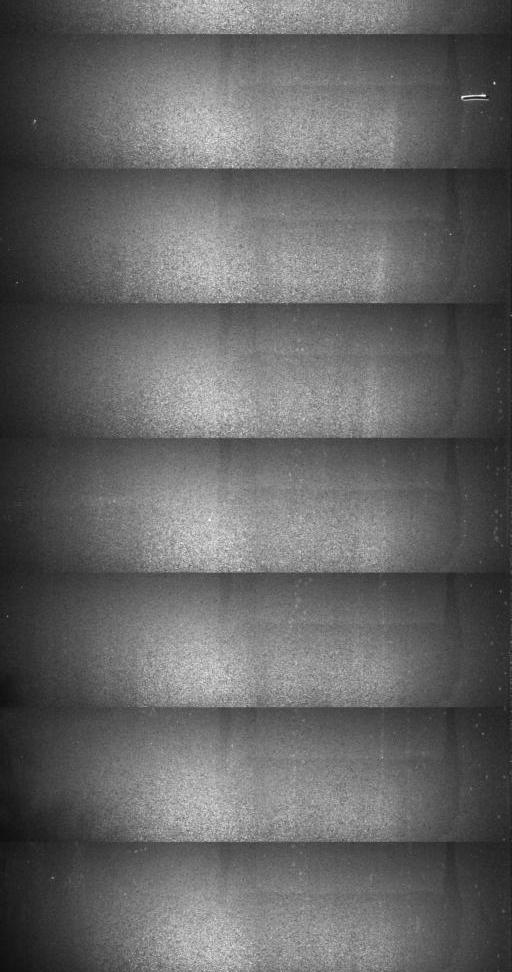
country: US
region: Vermont
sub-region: Franklin County
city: Richford
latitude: 44.9748
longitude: -72.5272
